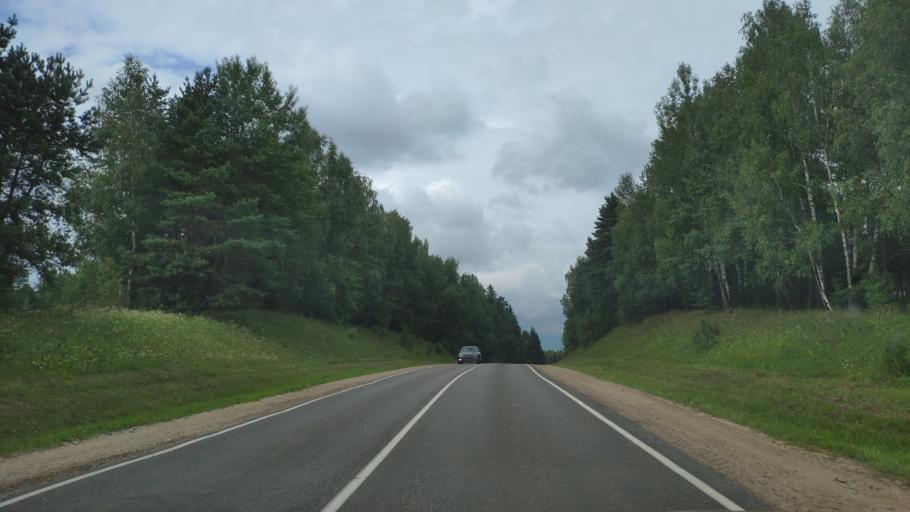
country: BY
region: Minsk
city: Novosel'ye
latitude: 53.9270
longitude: 27.2443
